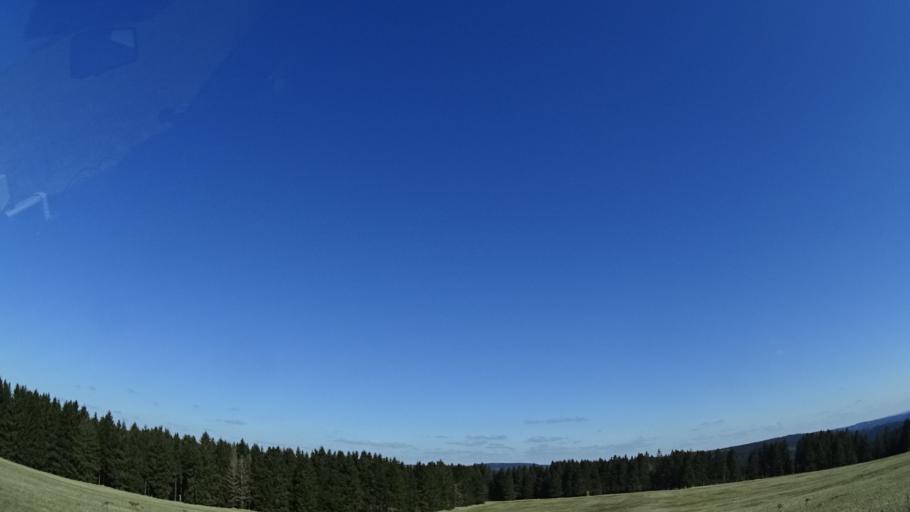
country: DE
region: Thuringia
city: Steinheid
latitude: 50.4576
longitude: 11.0992
